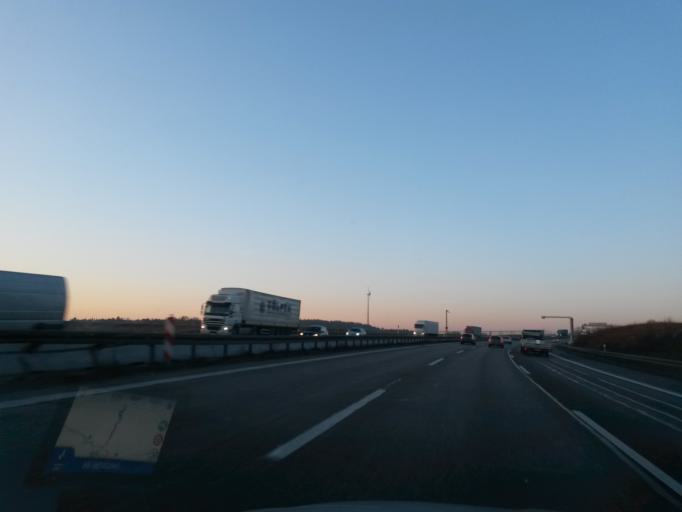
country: DE
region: Bavaria
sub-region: Upper Bavaria
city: Schweitenkirchen
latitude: 48.5352
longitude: 11.5950
